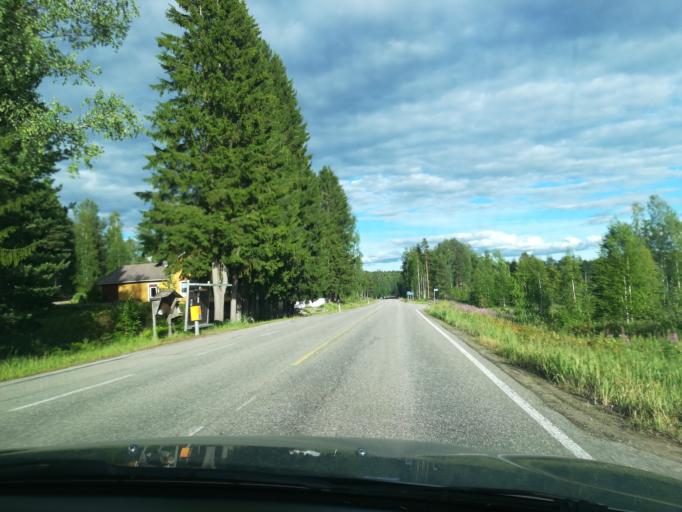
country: FI
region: South Karelia
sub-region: Lappeenranta
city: Savitaipale
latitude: 61.5313
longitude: 27.7389
